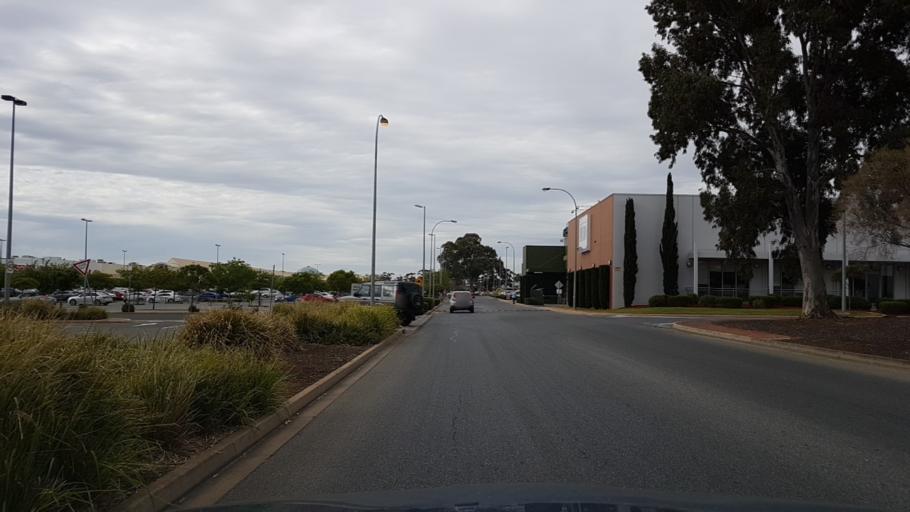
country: AU
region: South Australia
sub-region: Playford
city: Smithfield
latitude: -34.6914
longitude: 138.6874
